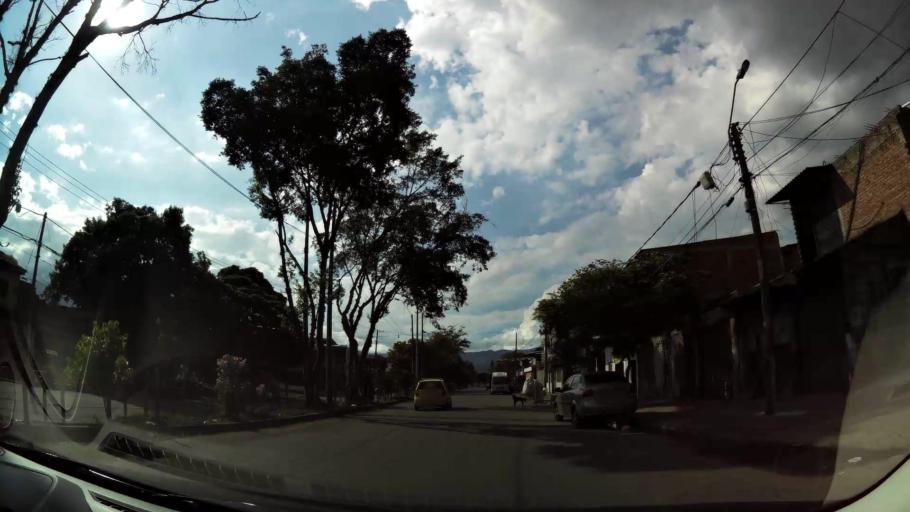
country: CO
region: Valle del Cauca
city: Cali
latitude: 3.4138
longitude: -76.5026
